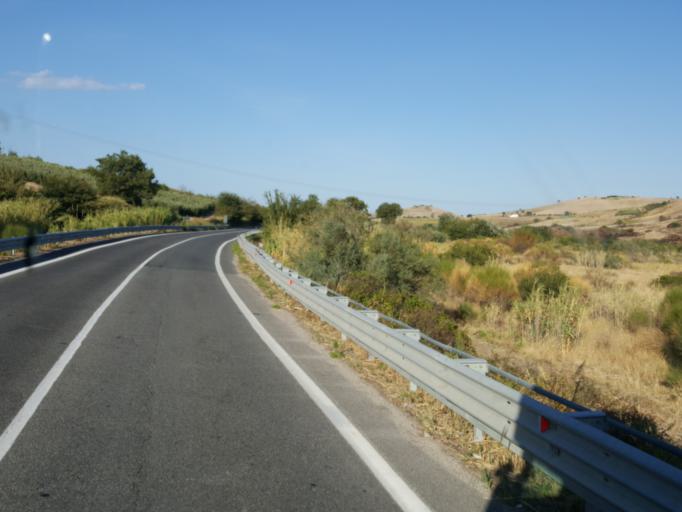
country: IT
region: Abruzzo
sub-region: Provincia di Chieti
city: Fresagrandinaria
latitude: 41.9691
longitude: 14.6893
